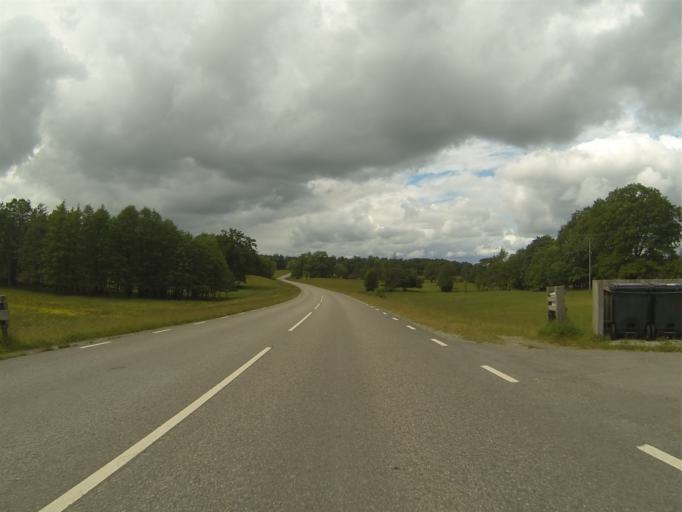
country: SE
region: Skane
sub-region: Lunds Kommun
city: Veberod
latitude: 55.6883
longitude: 13.4243
